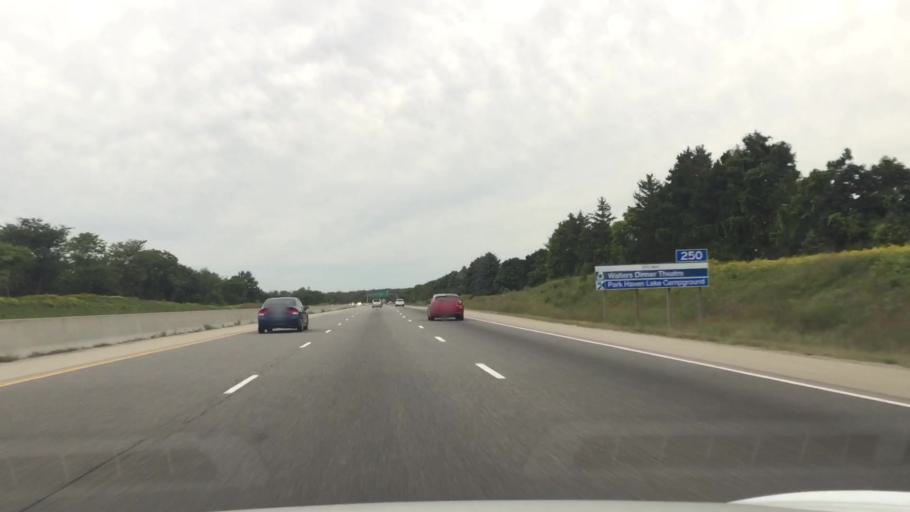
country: CA
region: Ontario
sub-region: Oxford County
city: Woodstock
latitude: 43.2379
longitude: -80.5824
